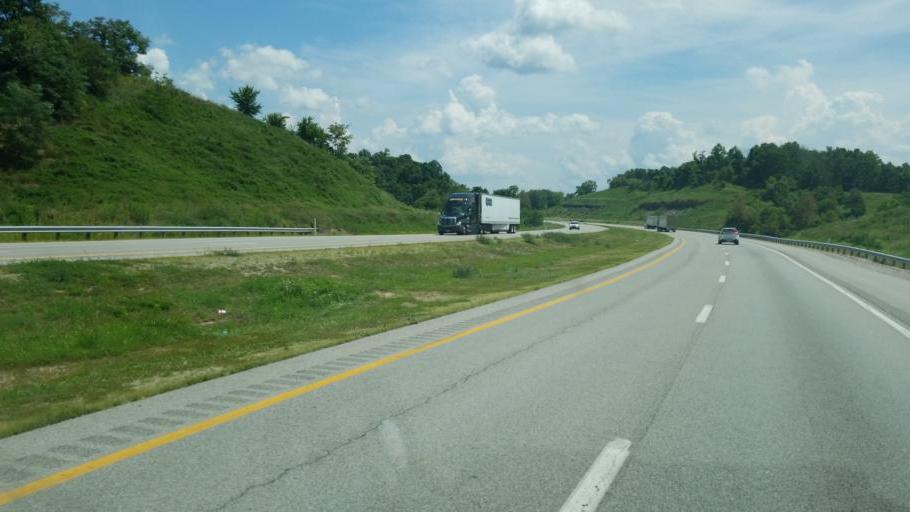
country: US
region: West Virginia
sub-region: Mason County
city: Point Pleasant
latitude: 38.7909
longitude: -82.0942
